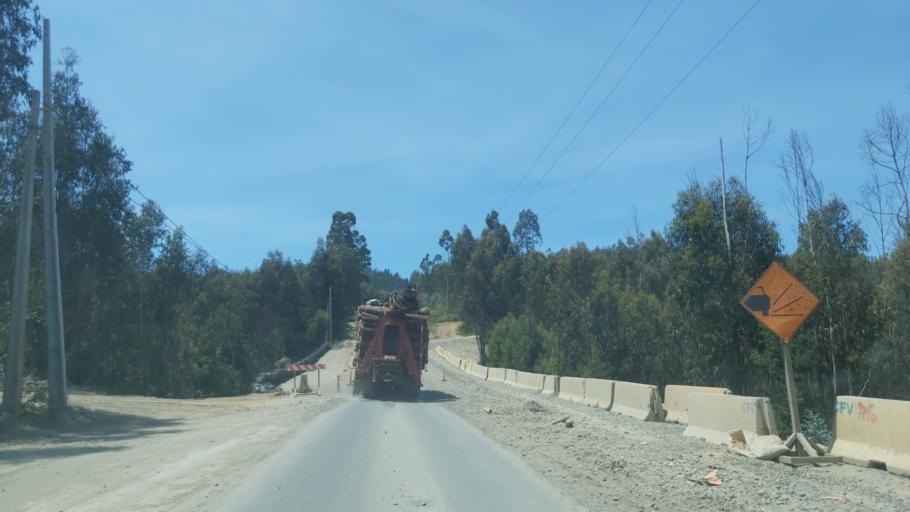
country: CL
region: Maule
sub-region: Provincia de Talca
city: Constitucion
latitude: -35.4455
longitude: -72.4664
